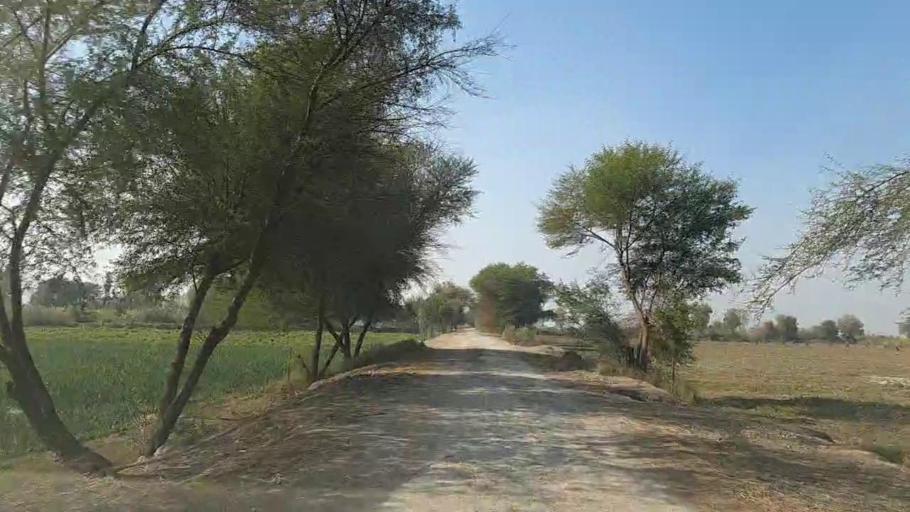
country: PK
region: Sindh
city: Daur
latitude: 26.5097
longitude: 68.3431
